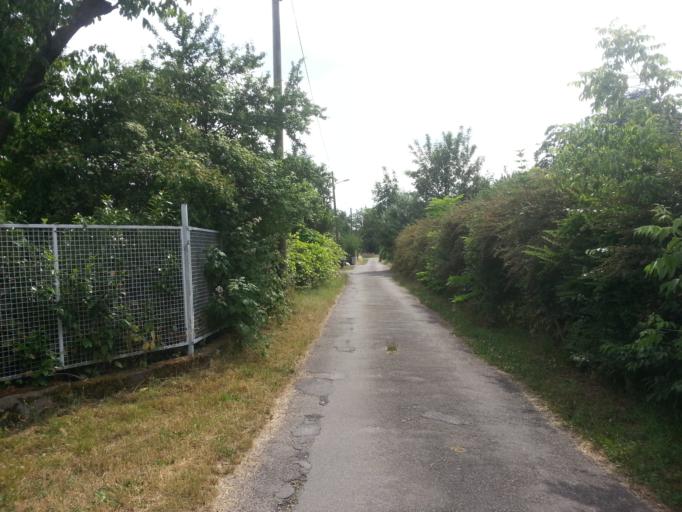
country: DE
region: Baden-Wuerttemberg
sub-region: Karlsruhe Region
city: Mannheim
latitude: 49.5228
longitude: 8.5267
